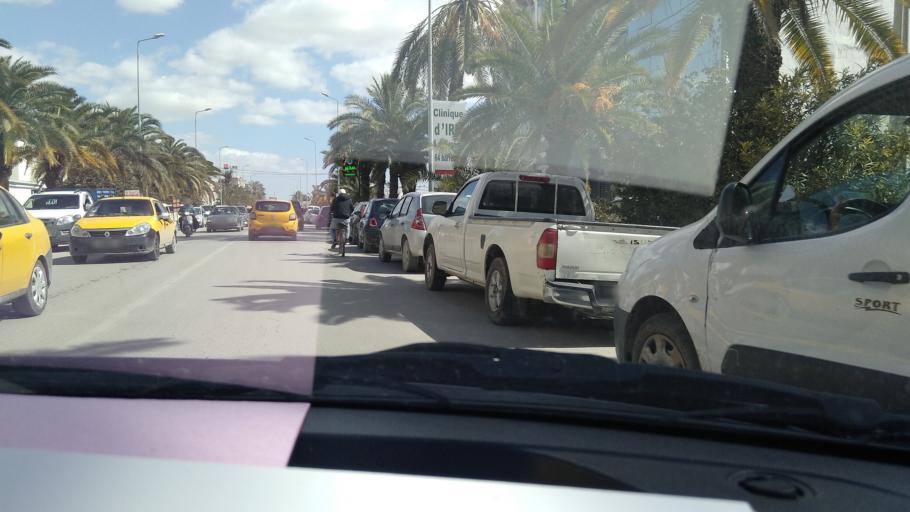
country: TN
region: Al Qayrawan
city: Kairouan
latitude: 35.6832
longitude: 10.0918
